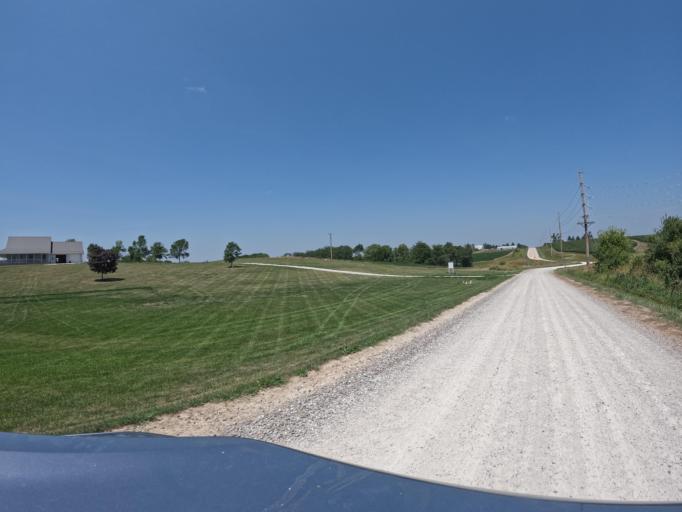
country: US
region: Iowa
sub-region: Keokuk County
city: Sigourney
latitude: 41.2753
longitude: -92.1806
